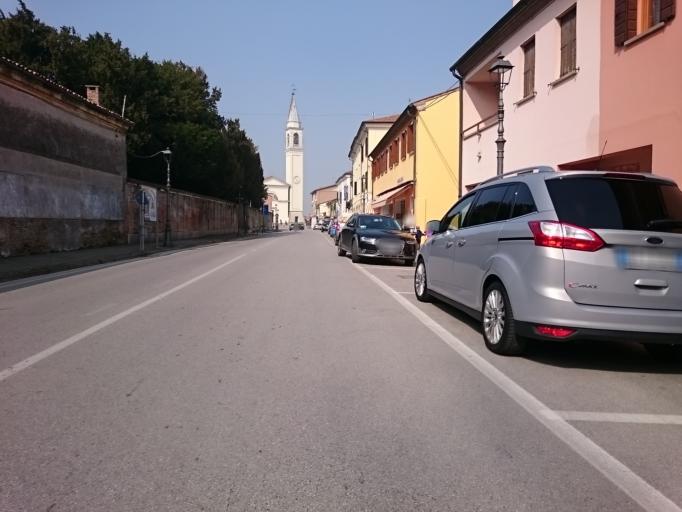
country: IT
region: Veneto
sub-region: Provincia di Padova
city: Pernumia
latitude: 45.2568
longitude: 11.7899
